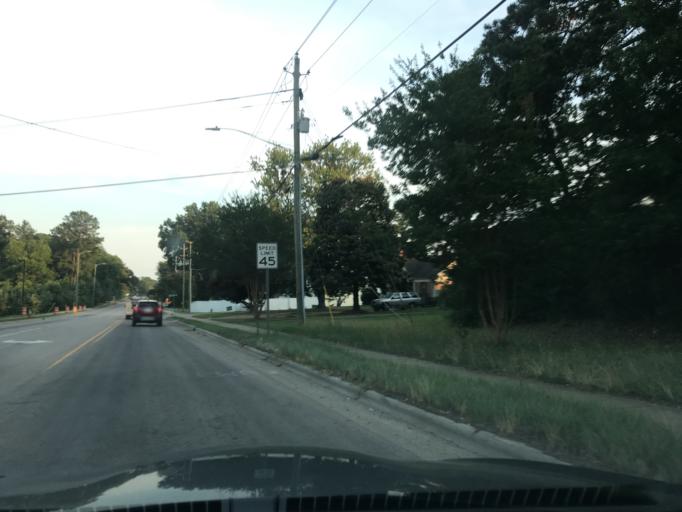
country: US
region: North Carolina
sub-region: Wake County
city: Raleigh
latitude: 35.7404
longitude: -78.6305
